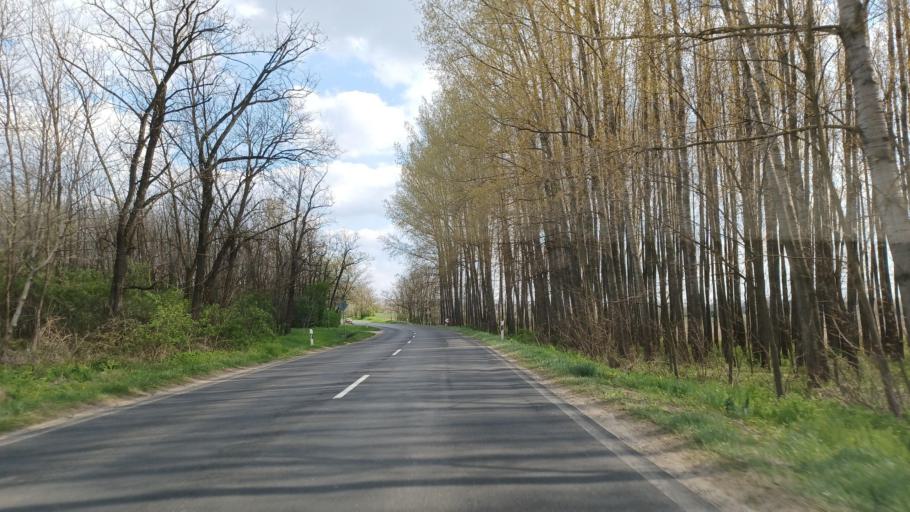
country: HU
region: Fejer
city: Cece
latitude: 46.7477
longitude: 18.6443
